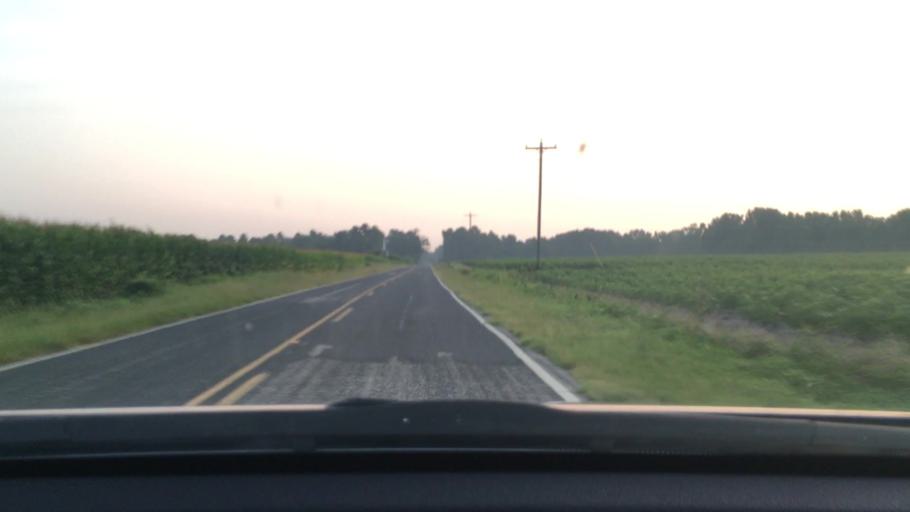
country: US
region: South Carolina
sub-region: Lee County
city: Bishopville
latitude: 34.1821
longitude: -80.1432
